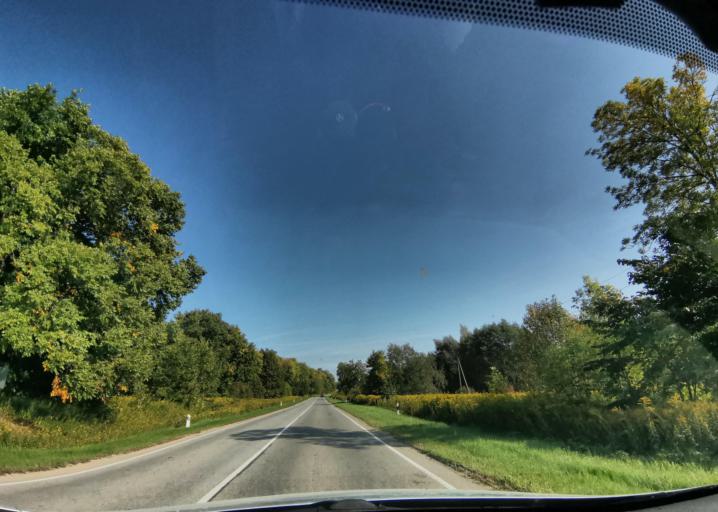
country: RU
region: Kaliningrad
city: Neman
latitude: 55.0183
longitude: 22.1018
